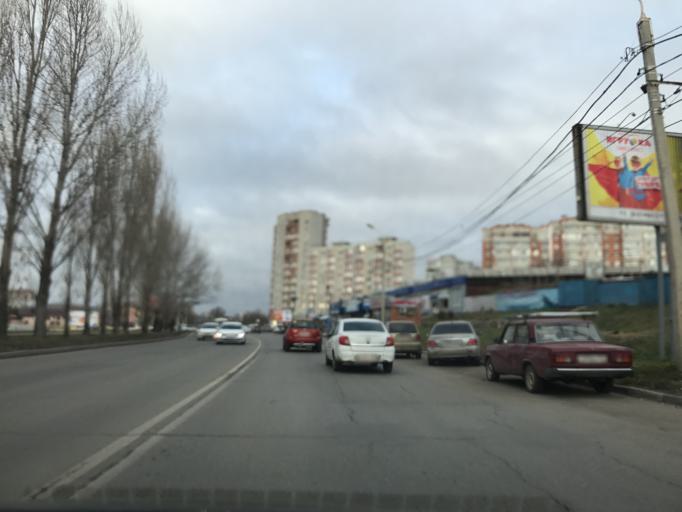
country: RU
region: Rostov
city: Temernik
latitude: 47.2923
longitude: 39.7347
